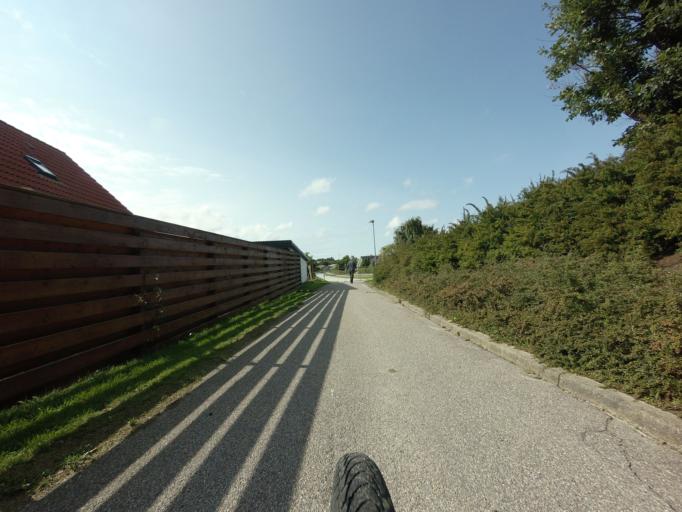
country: DK
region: North Denmark
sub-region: Hjorring Kommune
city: Hjorring
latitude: 57.5147
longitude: 10.0326
